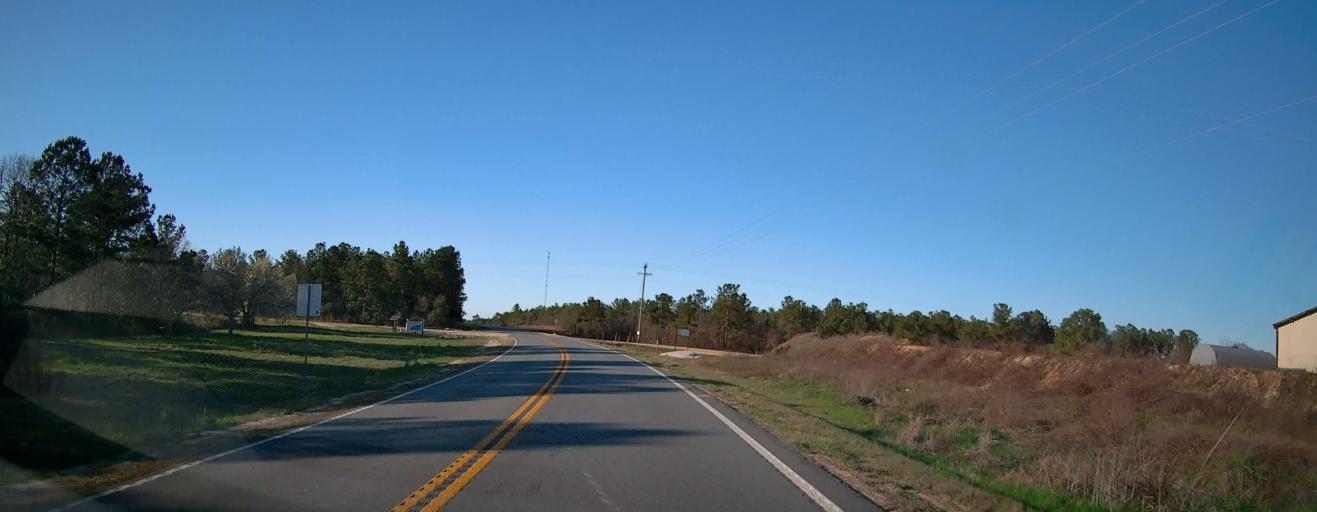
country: US
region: Georgia
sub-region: Talbot County
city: Talbotton
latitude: 32.5614
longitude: -84.4369
